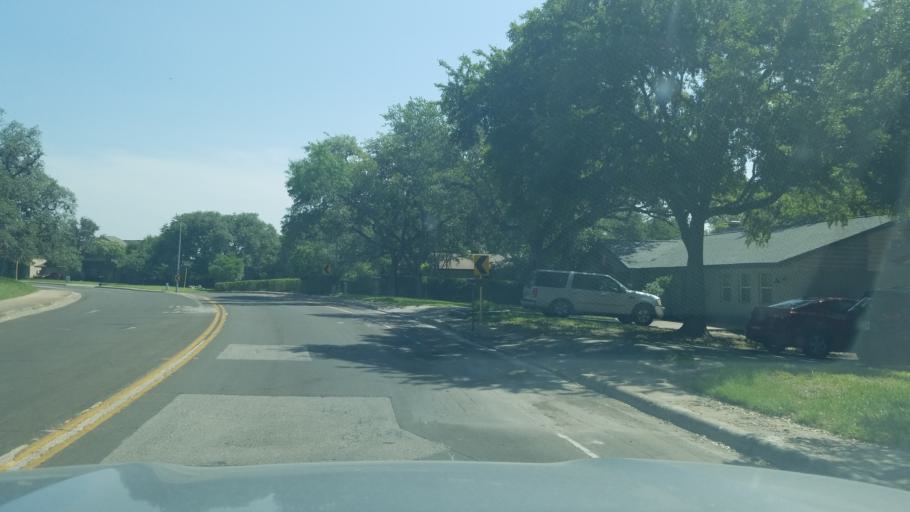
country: US
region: Texas
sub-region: Bexar County
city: Hollywood Park
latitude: 29.5793
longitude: -98.4641
